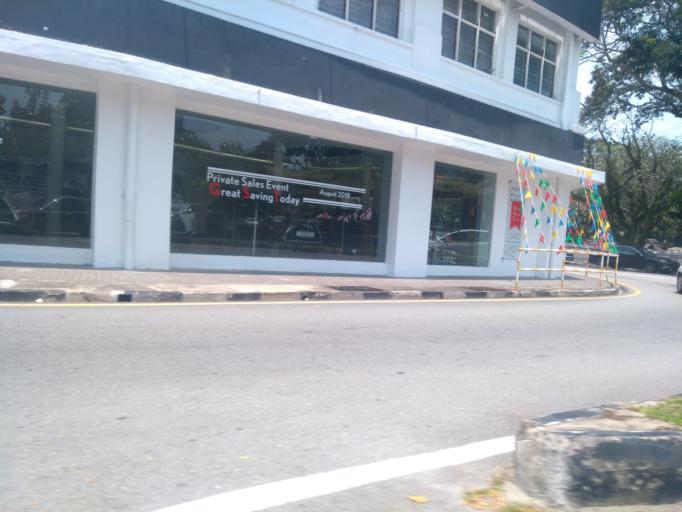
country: MY
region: Penang
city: George Town
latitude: 5.4234
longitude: 100.3332
